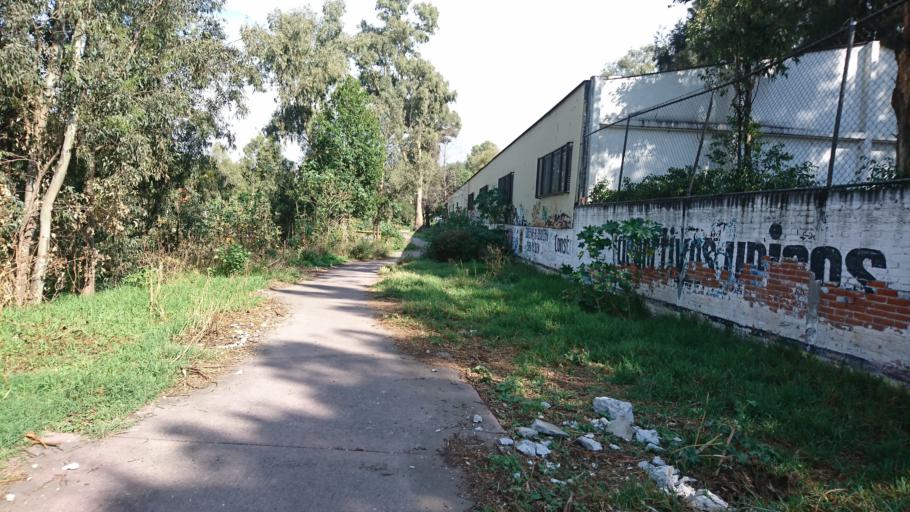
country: MX
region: Mexico City
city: Iztapalapa
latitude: 19.3307
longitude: -99.1094
